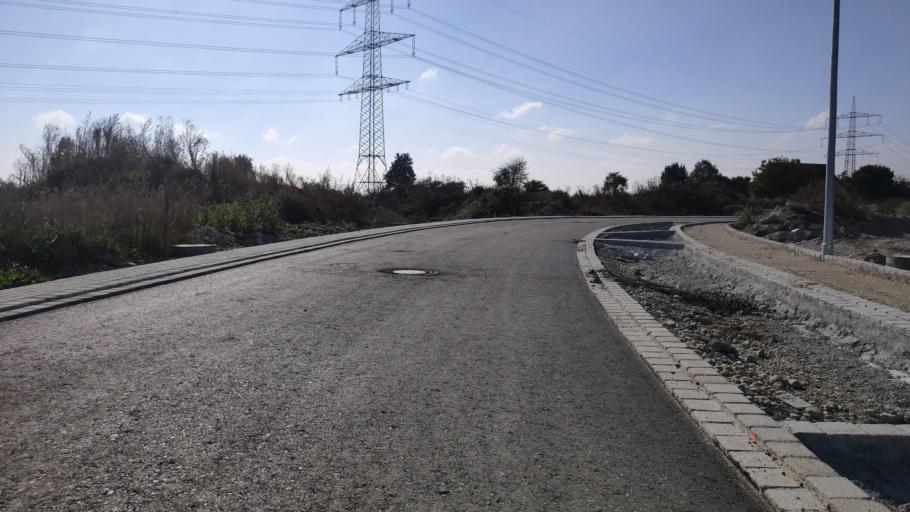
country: DE
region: Bavaria
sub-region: Swabia
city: Oberottmarshausen
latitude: 48.2331
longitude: 10.8615
